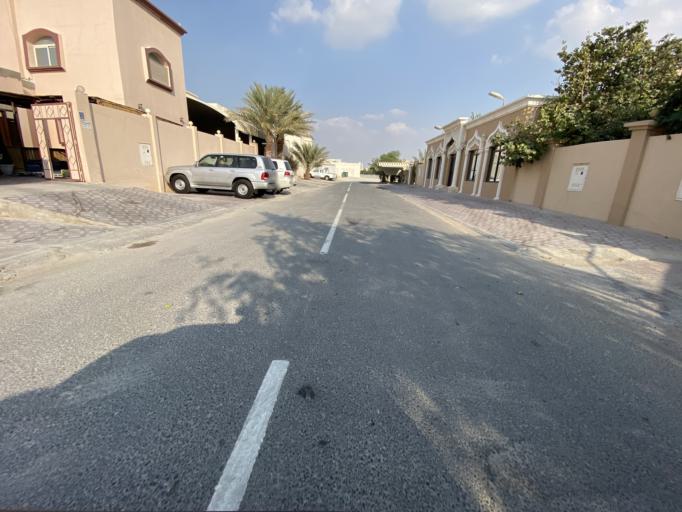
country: QA
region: Baladiyat ar Rayyan
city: Ar Rayyan
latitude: 25.2374
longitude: 51.3771
